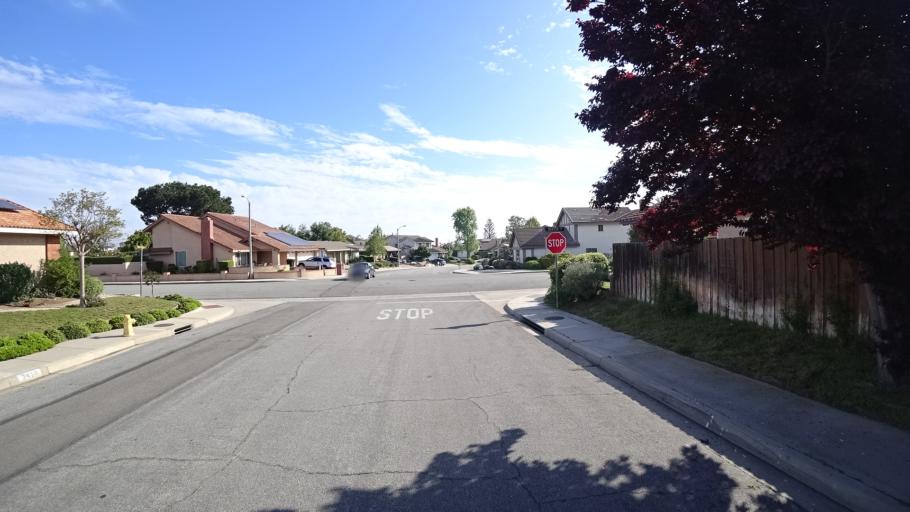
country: US
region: California
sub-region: Ventura County
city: Casa Conejo
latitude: 34.1730
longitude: -118.9490
